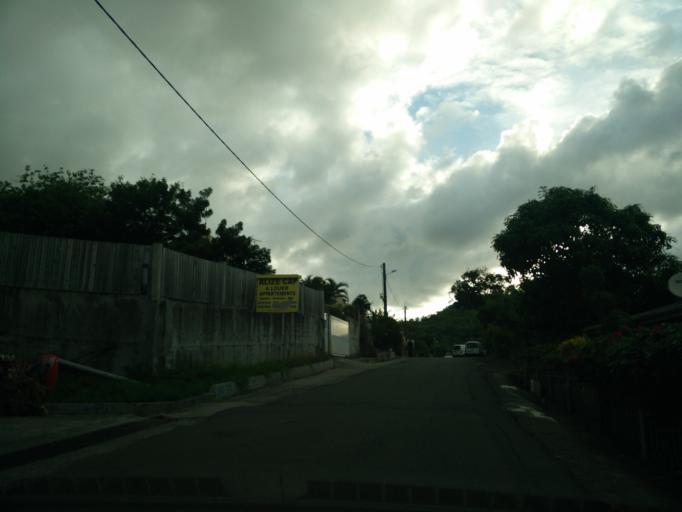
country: MQ
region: Martinique
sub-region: Martinique
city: Le Marin
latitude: 14.4599
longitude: -60.8452
